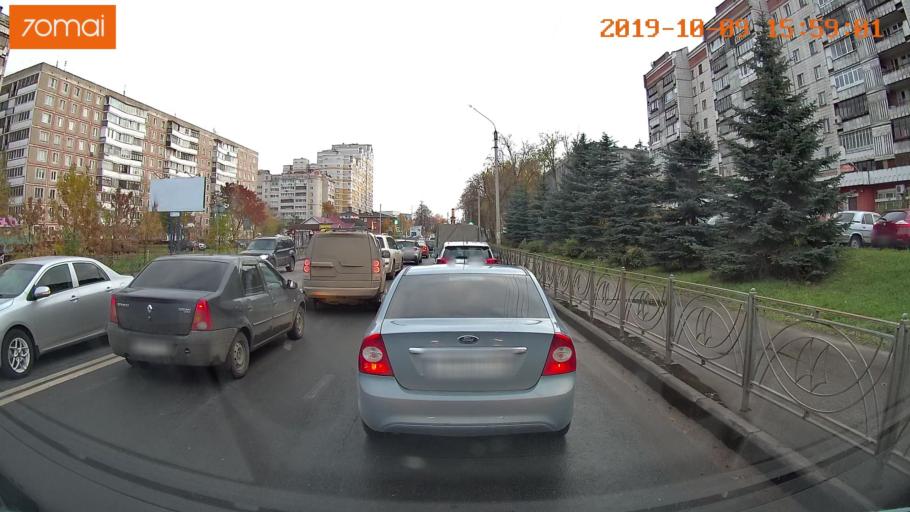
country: RU
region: Kostroma
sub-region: Kostromskoy Rayon
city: Kostroma
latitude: 57.7668
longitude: 40.9510
